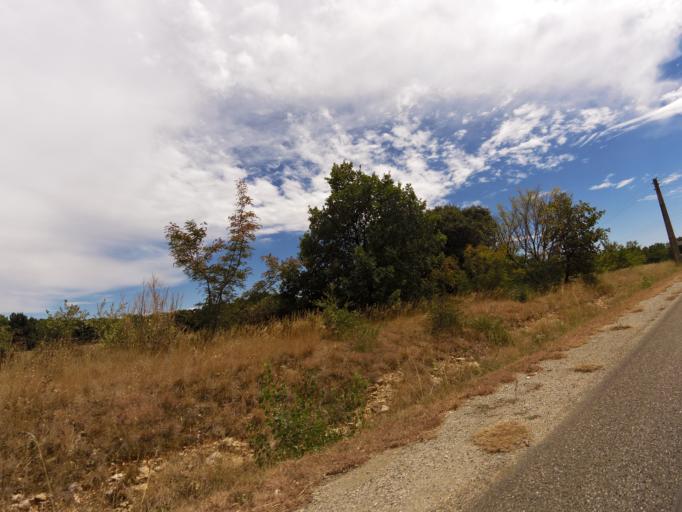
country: FR
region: Languedoc-Roussillon
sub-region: Departement du Gard
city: Quissac
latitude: 43.9293
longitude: 3.9796
